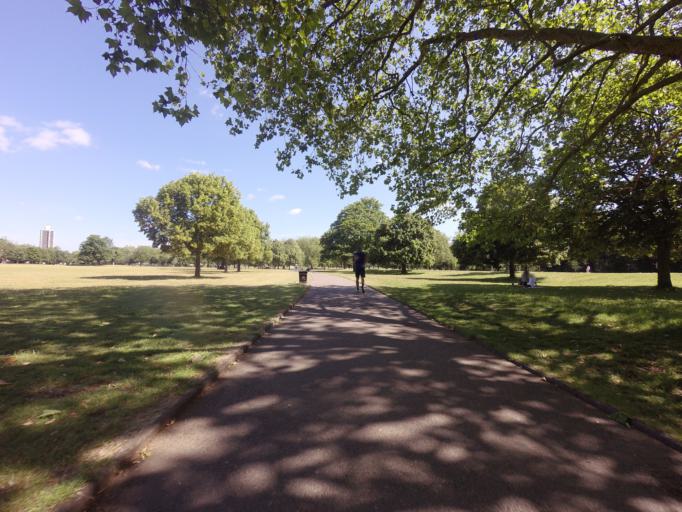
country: GB
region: England
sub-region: Greater London
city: East Ham
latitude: 51.5380
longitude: 0.0158
